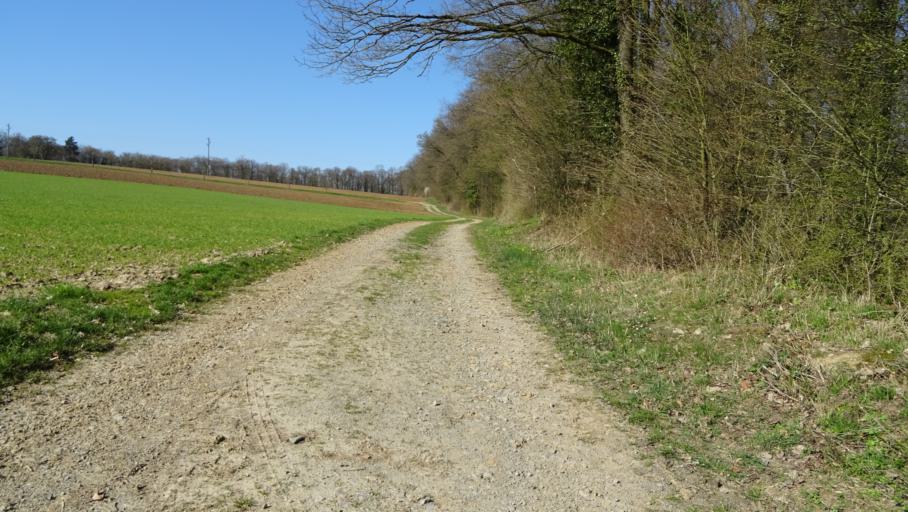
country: DE
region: Baden-Wuerttemberg
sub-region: Karlsruhe Region
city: Binau
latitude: 49.3608
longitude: 9.0415
